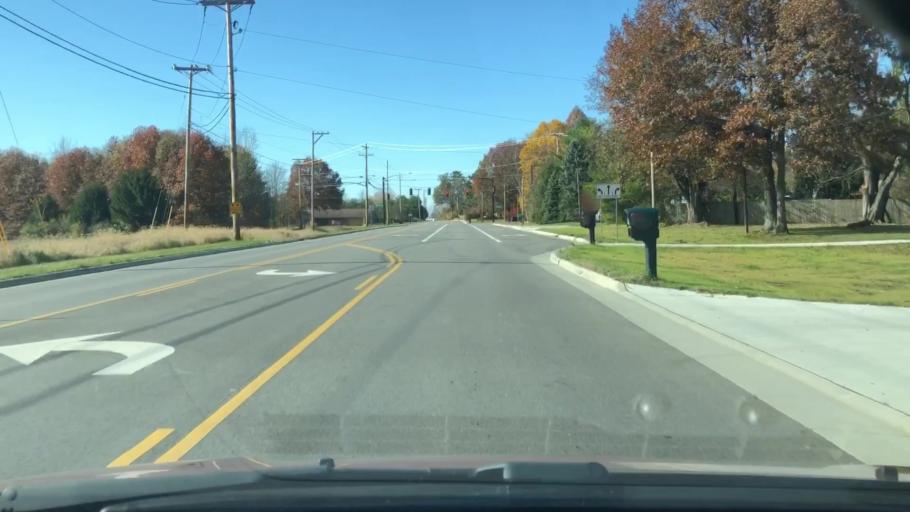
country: US
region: Ohio
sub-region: Franklin County
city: Westerville
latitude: 40.1826
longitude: -82.9235
